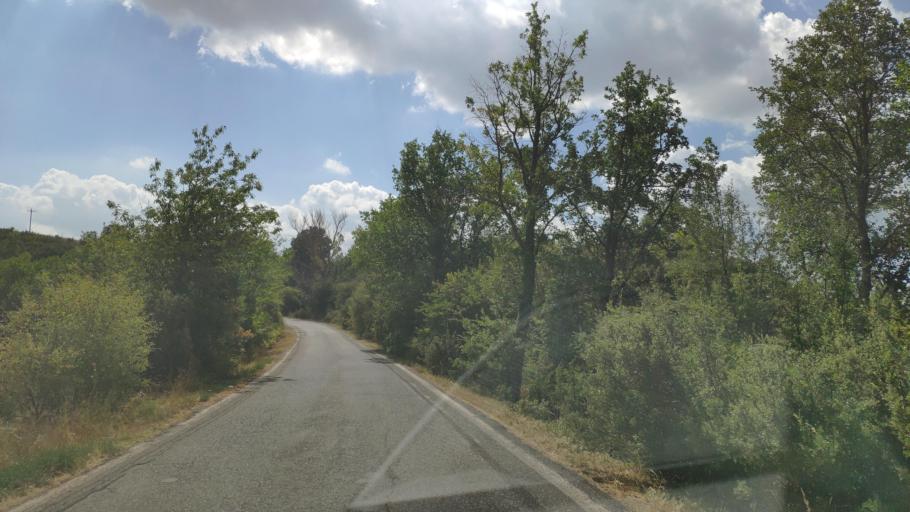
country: GR
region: Peloponnese
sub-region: Nomos Lakonias
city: Kariai
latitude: 37.3217
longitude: 22.4296
